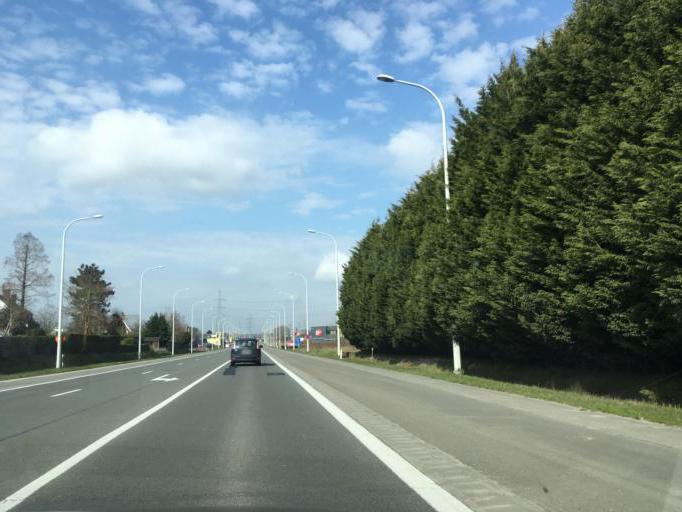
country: BE
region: Flanders
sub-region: Provincie West-Vlaanderen
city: Lendelede
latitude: 50.8907
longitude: 3.2452
